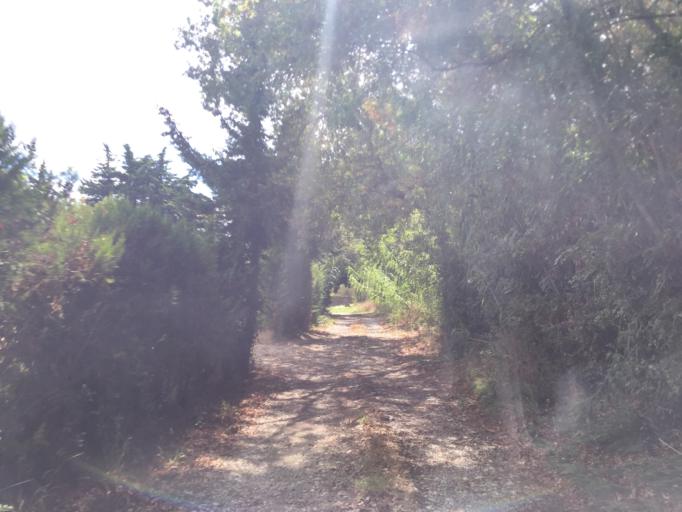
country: FR
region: Provence-Alpes-Cote d'Azur
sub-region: Departement du Vaucluse
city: Caderousse
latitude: 44.1040
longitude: 4.7666
